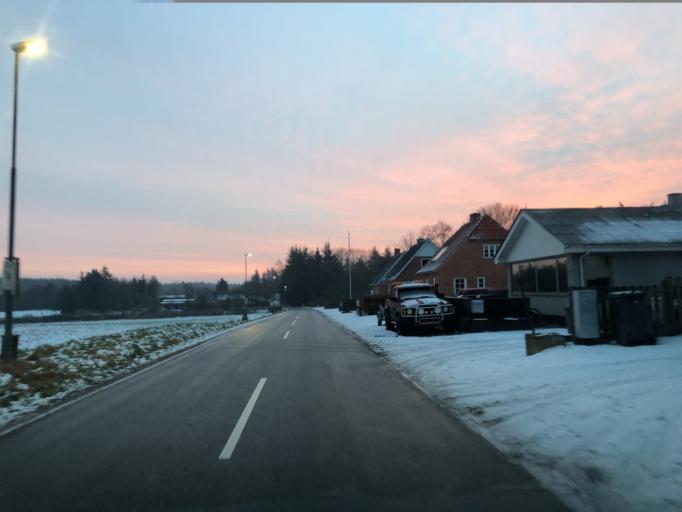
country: DK
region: Central Jutland
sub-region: Holstebro Kommune
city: Ulfborg
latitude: 56.2012
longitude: 8.4286
